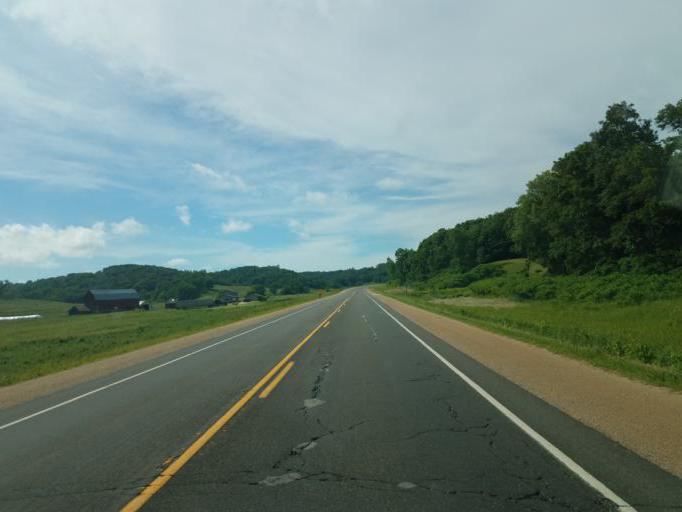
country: US
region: Wisconsin
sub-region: Monroe County
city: Tomah
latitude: 43.8728
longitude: -90.4772
